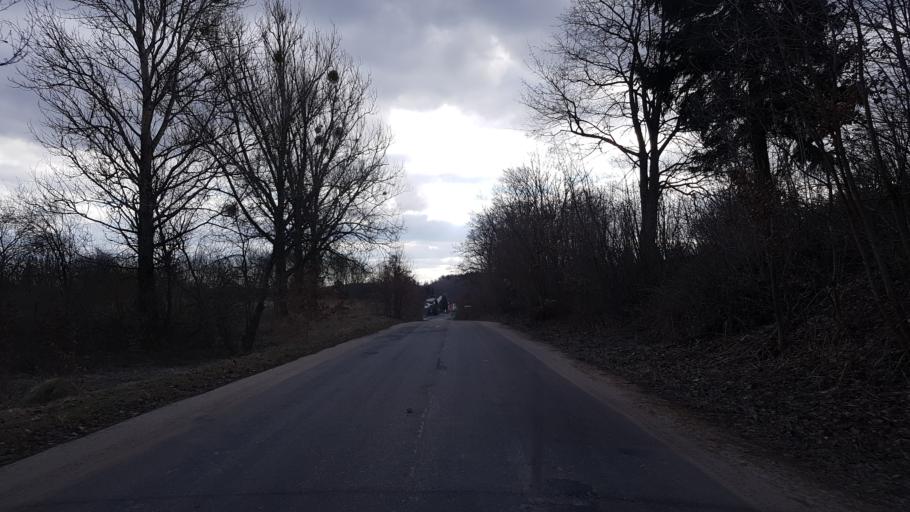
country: PL
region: West Pomeranian Voivodeship
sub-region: Powiat koszalinski
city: Bobolice
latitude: 53.9817
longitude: 16.5378
